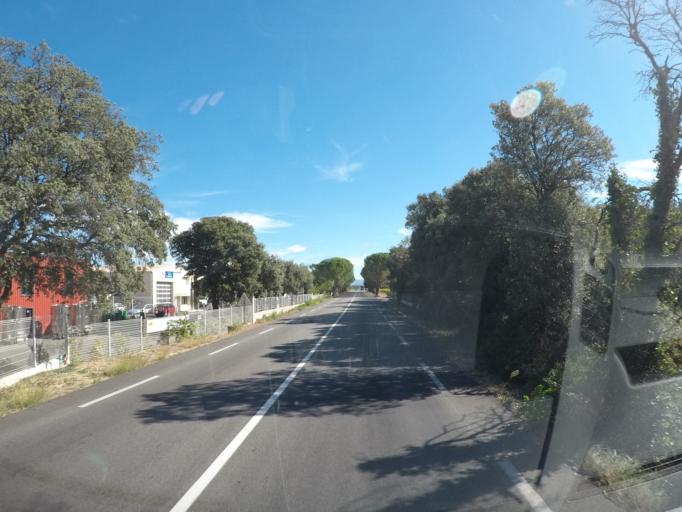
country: FR
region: Rhone-Alpes
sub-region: Departement de la Drome
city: Suze-la-Rousse
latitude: 44.2881
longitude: 4.8467
